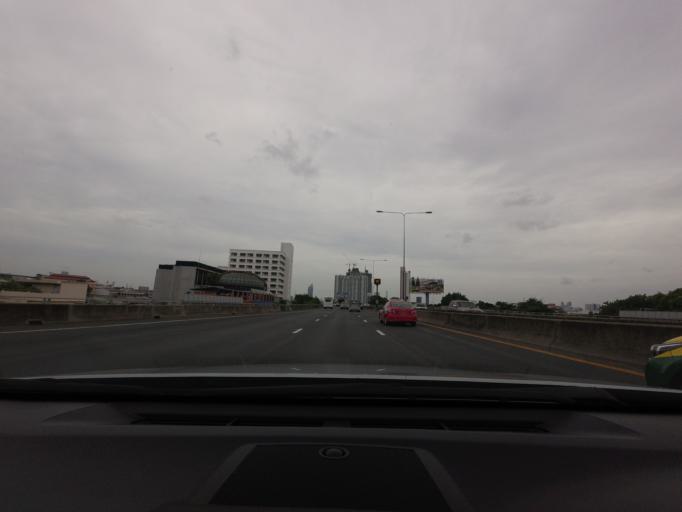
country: TH
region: Bangkok
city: Sathon
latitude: 13.7080
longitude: 100.5189
